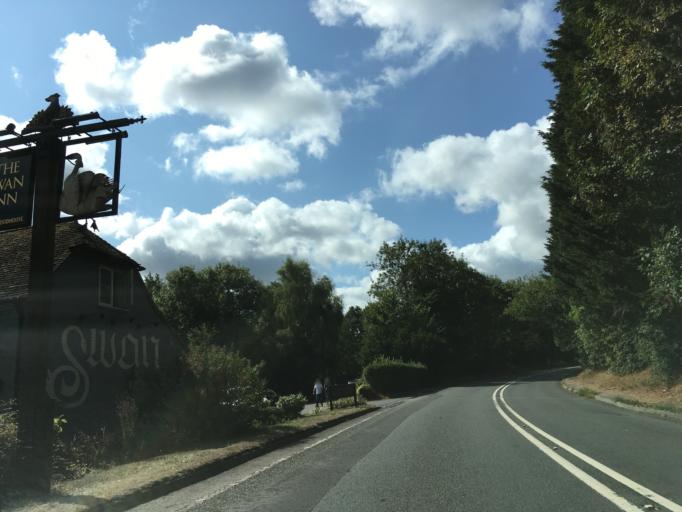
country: GB
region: England
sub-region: West Berkshire
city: Greenham
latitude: 51.3725
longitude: -1.3167
